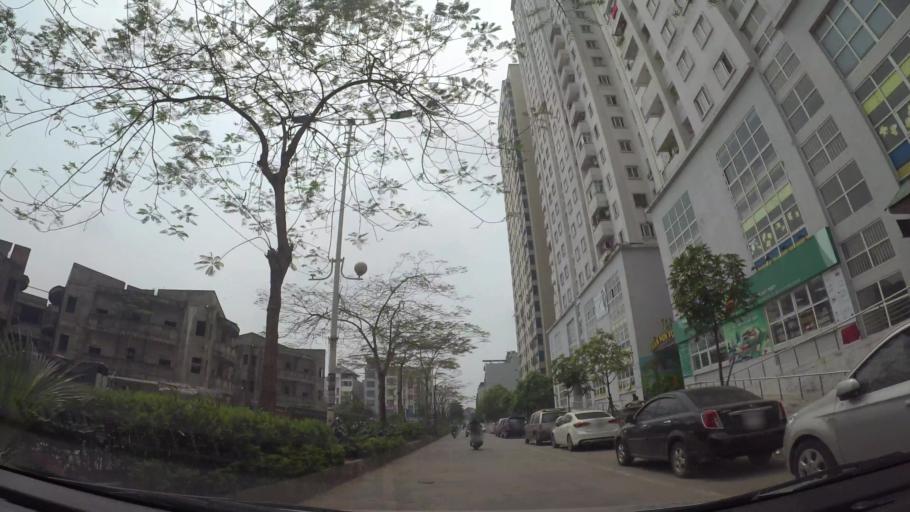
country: VN
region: Ha Noi
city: Ha Dong
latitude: 20.9734
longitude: 105.7637
